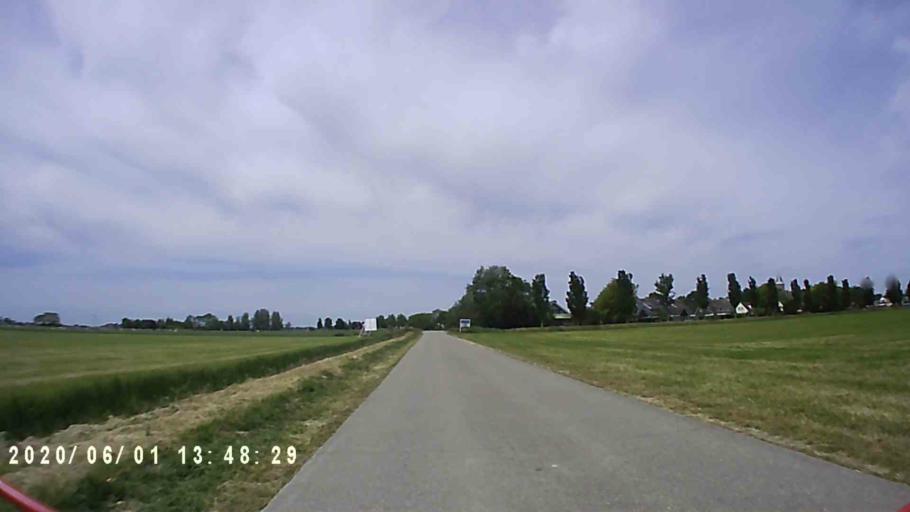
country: NL
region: Friesland
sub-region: Gemeente Littenseradiel
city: Wommels
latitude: 53.0928
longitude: 5.6205
